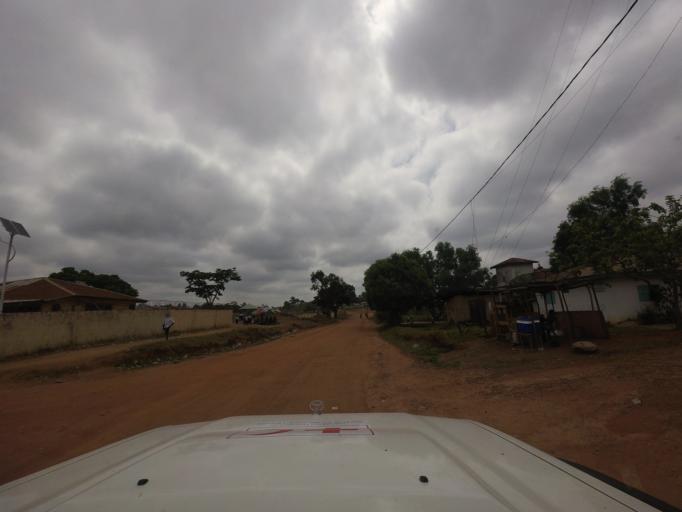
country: LR
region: Lofa
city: Voinjama
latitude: 8.4210
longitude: -9.7487
